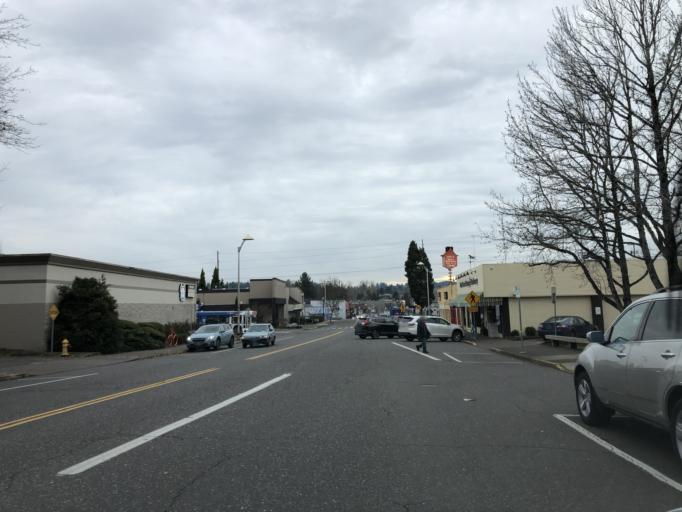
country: US
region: Oregon
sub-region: Washington County
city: Tigard
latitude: 45.4318
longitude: -122.7695
